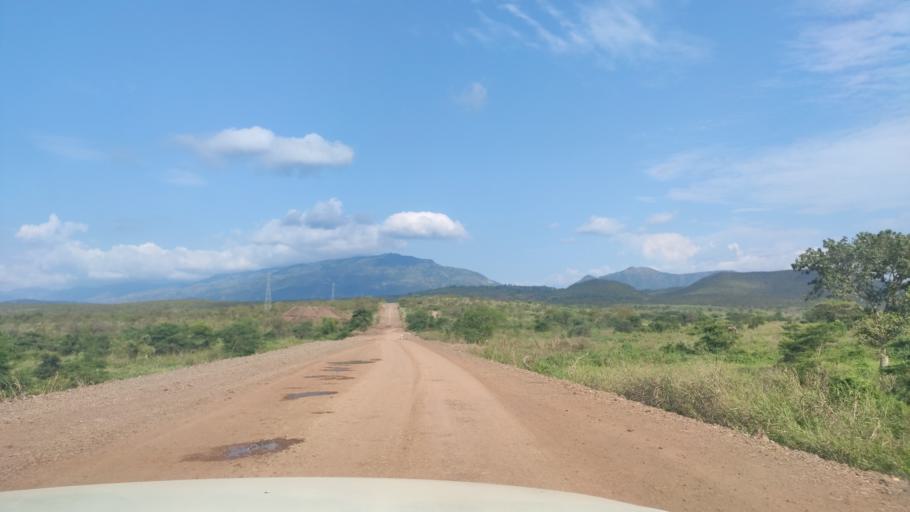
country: ET
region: Southern Nations, Nationalities, and People's Region
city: Felege Neway
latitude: 6.4341
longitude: 37.2675
